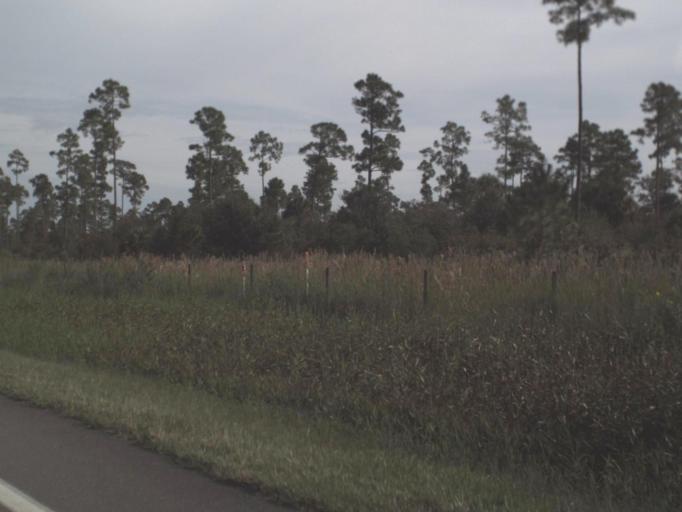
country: US
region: Florida
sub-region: Lee County
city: Olga
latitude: 26.9307
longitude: -81.7606
